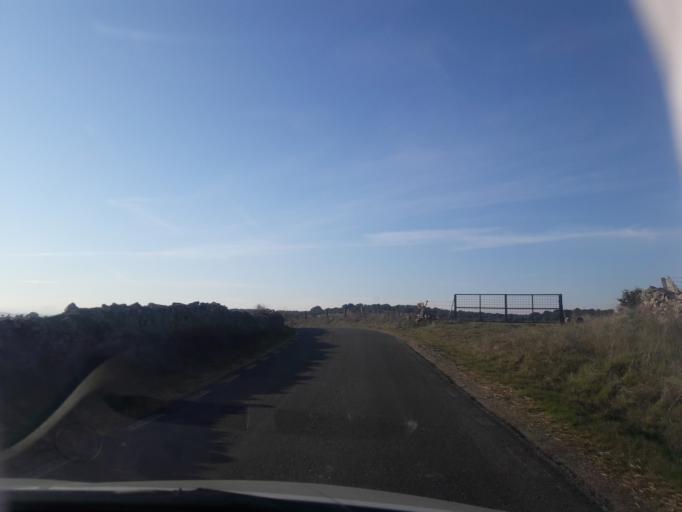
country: ES
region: Castille and Leon
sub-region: Provincia de Salamanca
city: Montejo
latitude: 40.6293
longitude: -5.6203
